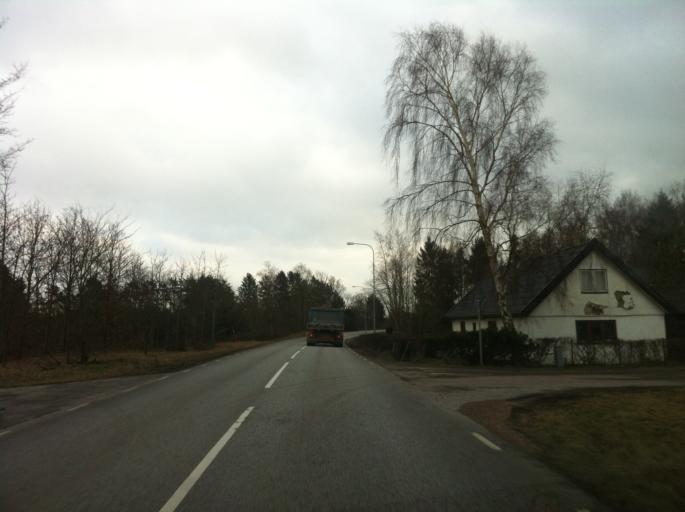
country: SE
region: Skane
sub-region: Kavlinge Kommun
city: Hofterup
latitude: 55.8338
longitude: 12.9693
